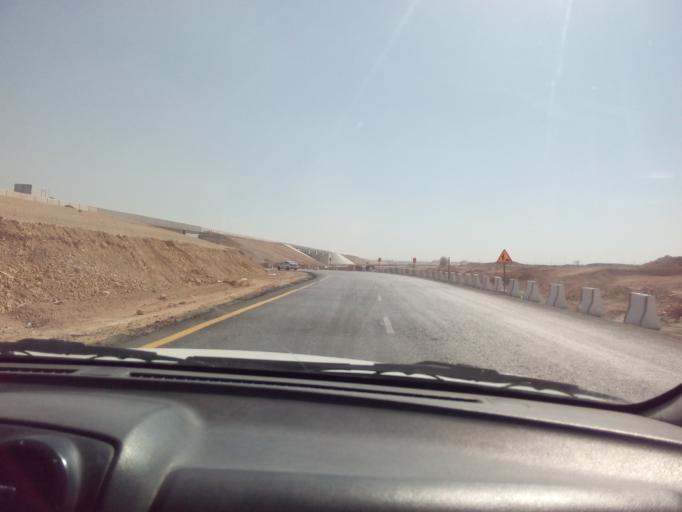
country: SA
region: Ar Riyad
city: Riyadh
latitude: 24.5959
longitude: 46.8861
